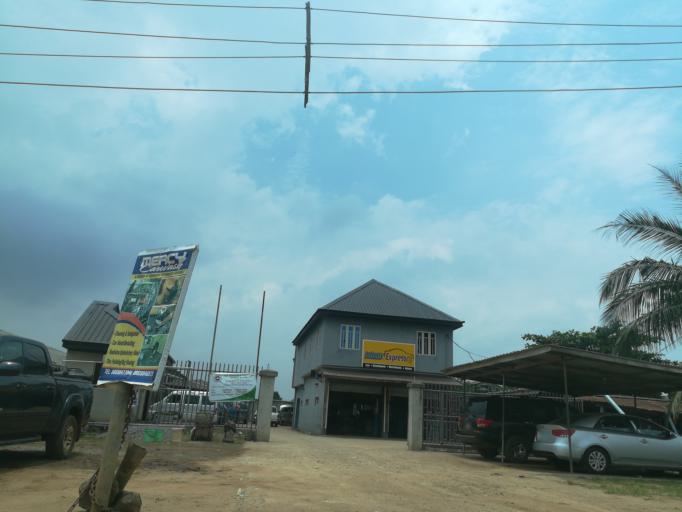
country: NG
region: Lagos
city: Ikorodu
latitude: 6.6185
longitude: 3.5621
